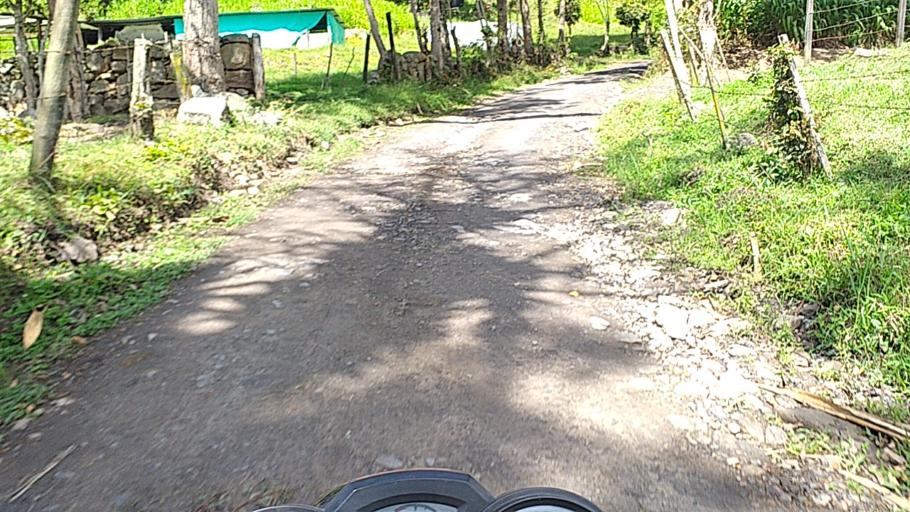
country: CO
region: Cundinamarca
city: Tenza
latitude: 5.1084
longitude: -73.4517
